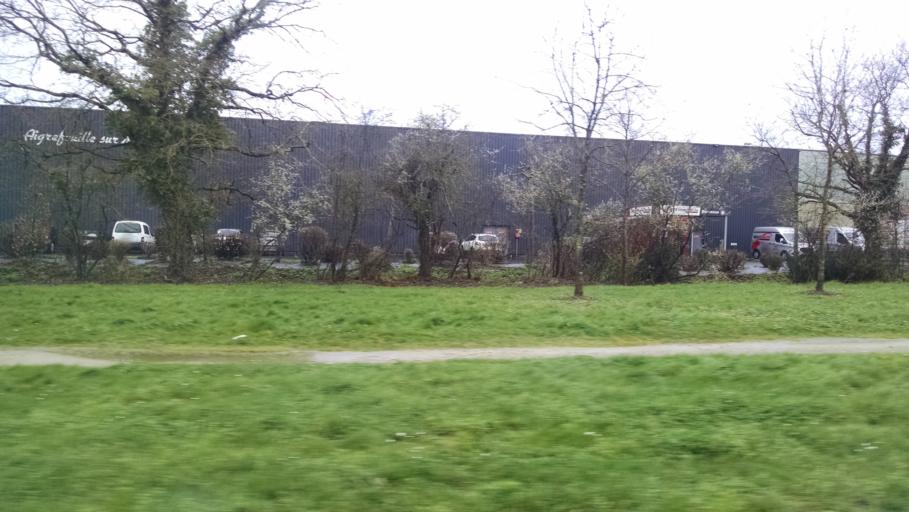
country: FR
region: Pays de la Loire
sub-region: Departement de la Loire-Atlantique
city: Aigrefeuille-sur-Maine
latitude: 47.0828
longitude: -1.4091
